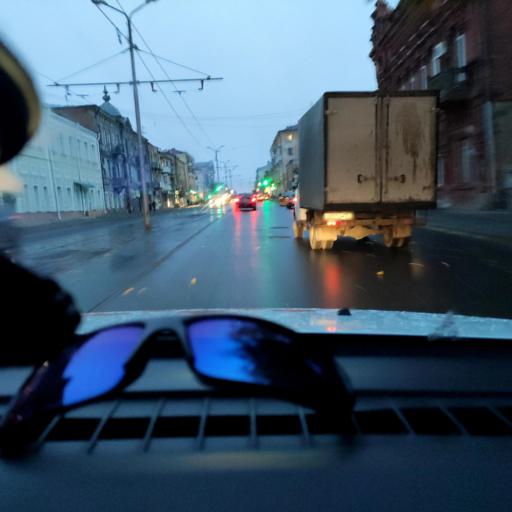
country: RU
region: Samara
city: Rozhdestveno
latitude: 53.1836
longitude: 50.0893
